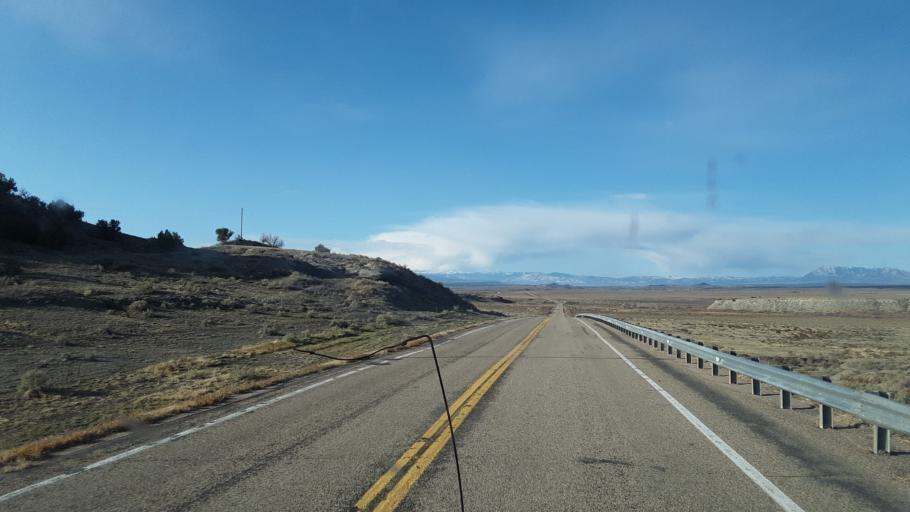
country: US
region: Colorado
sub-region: Huerfano County
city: Walsenburg
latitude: 37.6915
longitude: -104.6328
